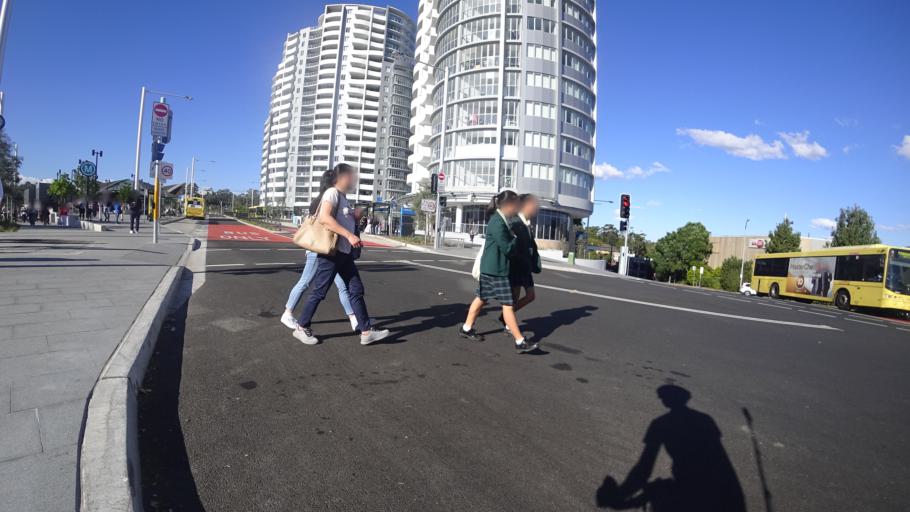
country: AU
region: New South Wales
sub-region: The Hills Shire
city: Castle Hill
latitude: -33.7321
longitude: 151.0060
